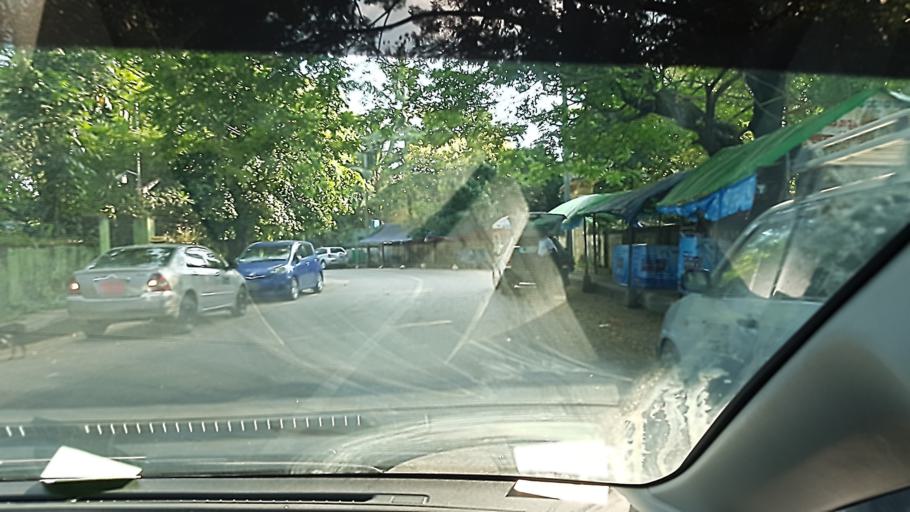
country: MM
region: Yangon
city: Yangon
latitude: 16.8126
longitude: 96.1653
